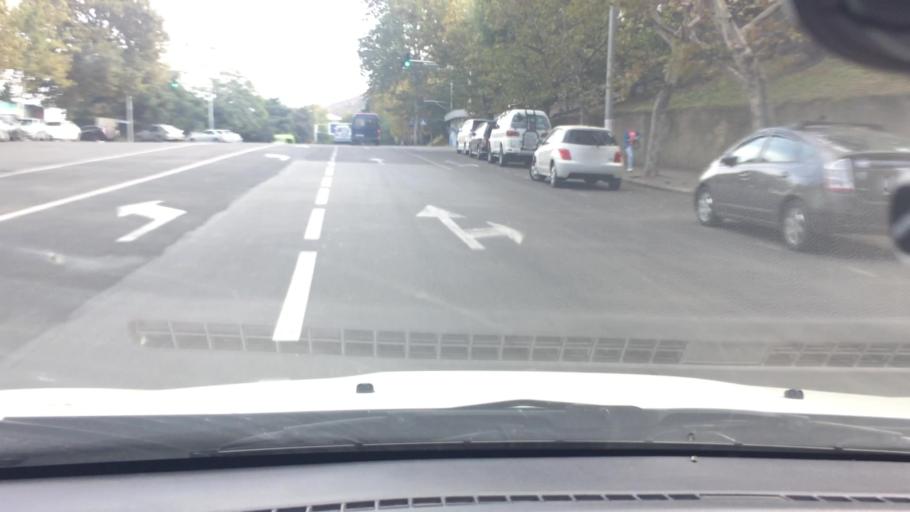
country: GE
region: T'bilisi
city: Tbilisi
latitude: 41.6727
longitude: 44.8337
